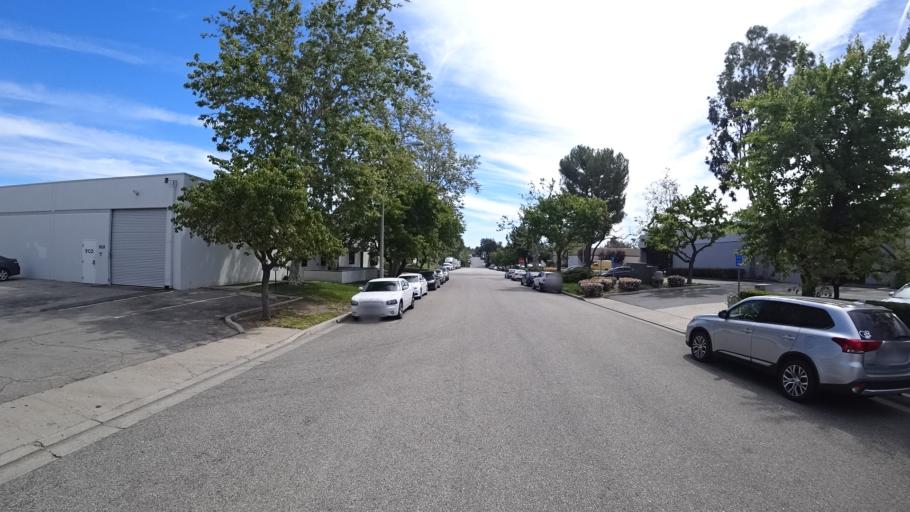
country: US
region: California
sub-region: Ventura County
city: Casa Conejo
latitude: 34.1928
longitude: -118.9323
